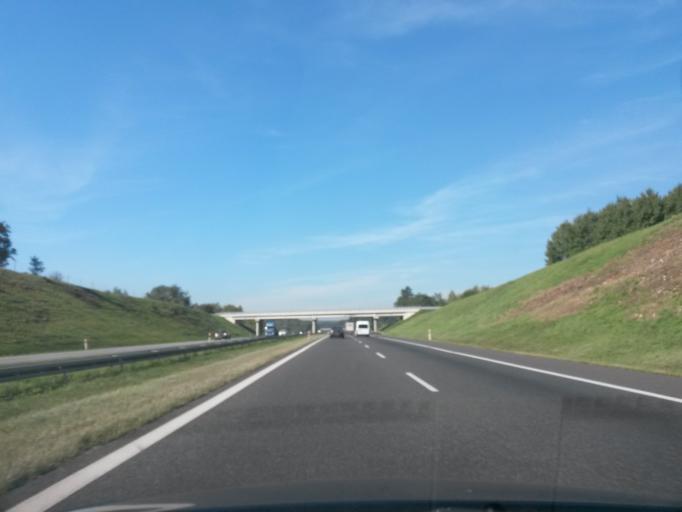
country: PL
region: Lesser Poland Voivodeship
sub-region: Powiat krakowski
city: Czulow
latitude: 50.0841
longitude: 19.7003
